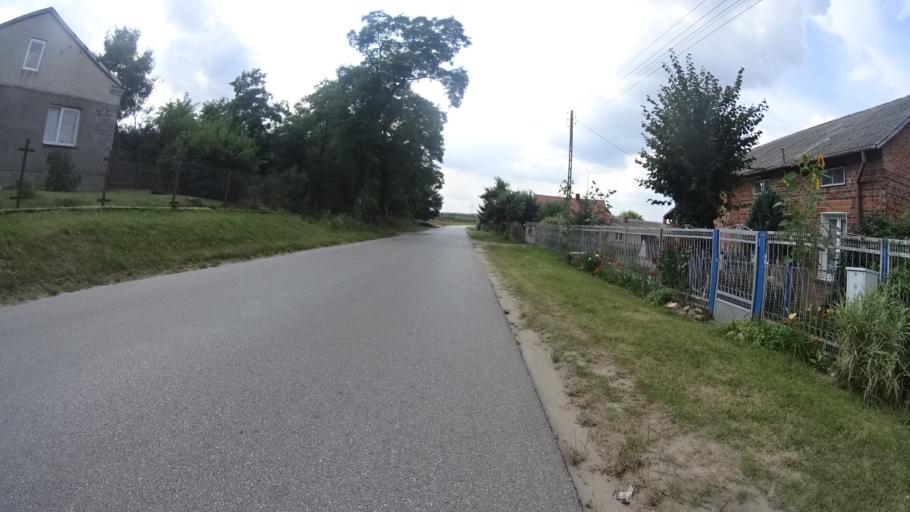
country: PL
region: Masovian Voivodeship
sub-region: Powiat grojecki
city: Mogielnica
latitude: 51.6589
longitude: 20.7514
